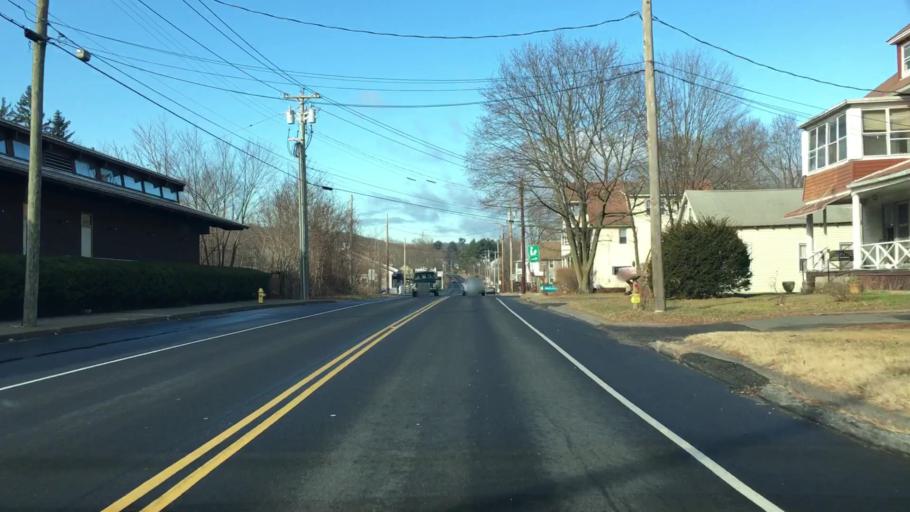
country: US
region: Connecticut
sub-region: Fairfield County
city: Shelton
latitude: 41.3280
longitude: -73.1035
